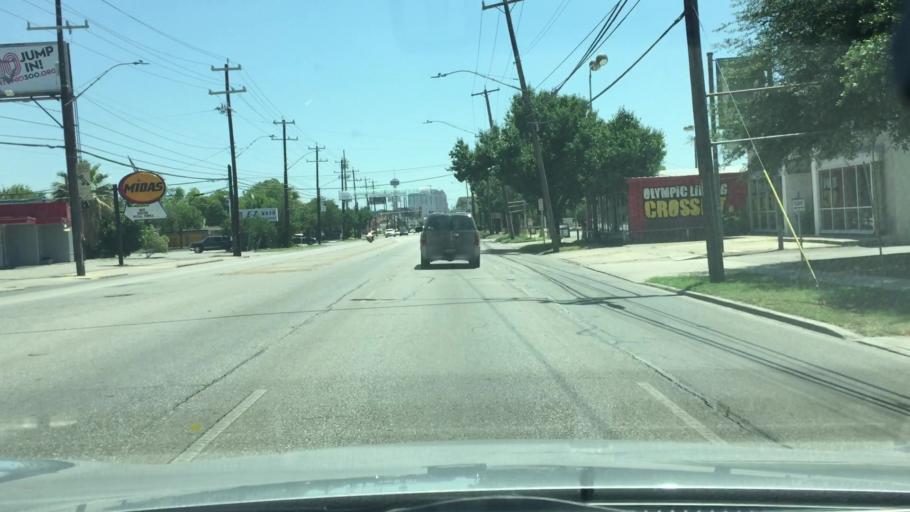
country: US
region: Texas
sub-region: Bexar County
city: San Antonio
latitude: 29.4495
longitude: -98.4745
